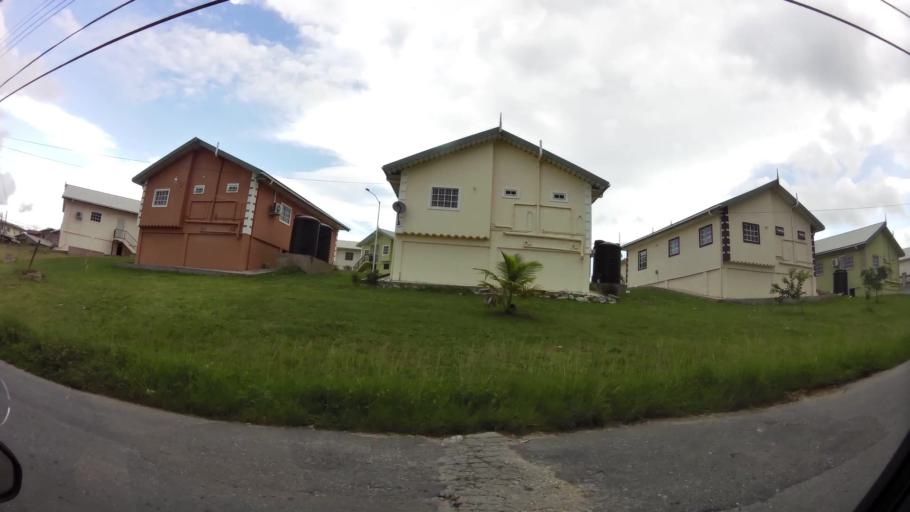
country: TT
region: City of San Fernando
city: Mon Repos
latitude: 10.2510
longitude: -61.4562
